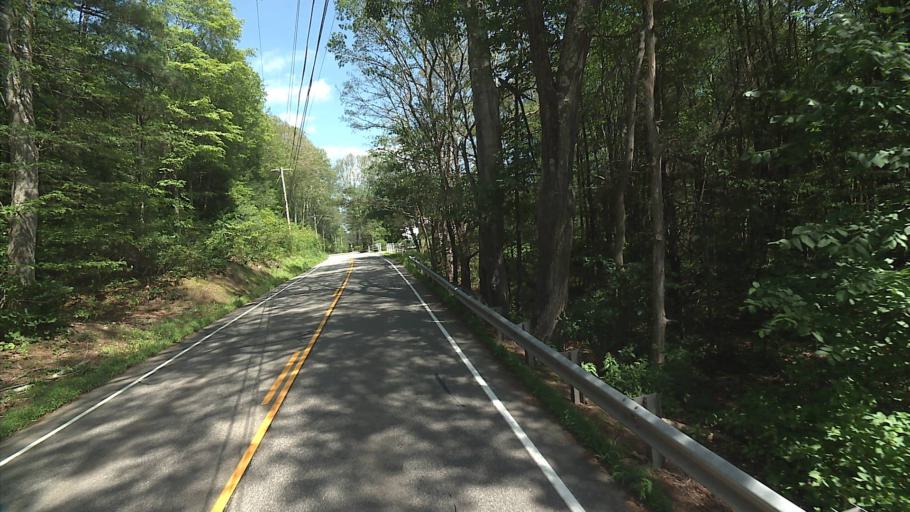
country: US
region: Connecticut
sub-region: Windham County
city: South Woodstock
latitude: 41.9126
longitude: -72.0777
